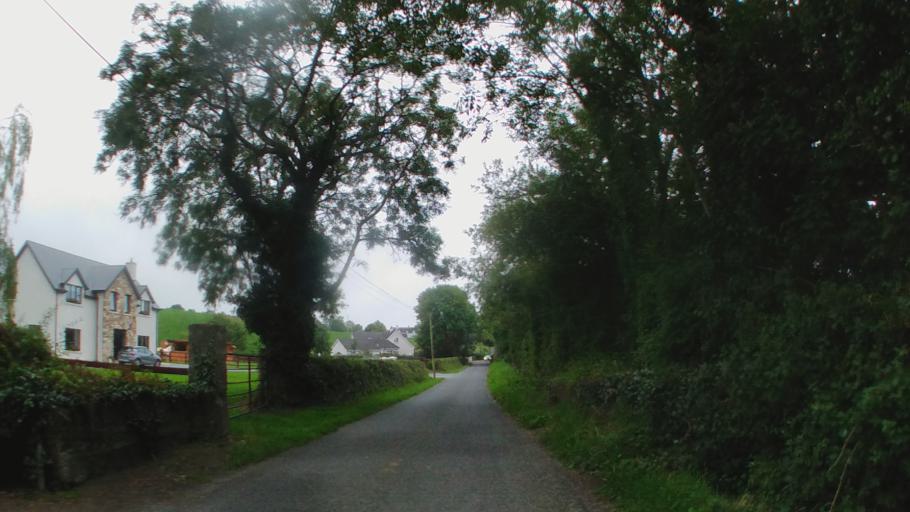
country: IE
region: Leinster
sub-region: Kilkenny
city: Kilkenny
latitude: 52.7045
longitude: -7.1924
